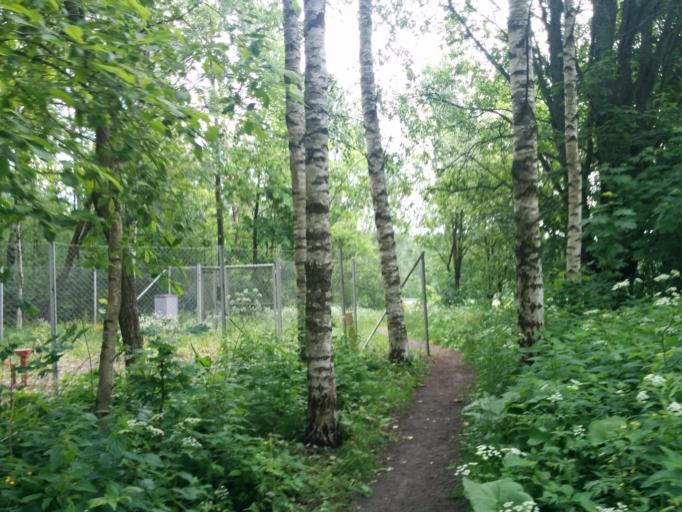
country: FI
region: Uusimaa
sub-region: Helsinki
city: Vantaa
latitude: 60.2372
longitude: 25.1333
